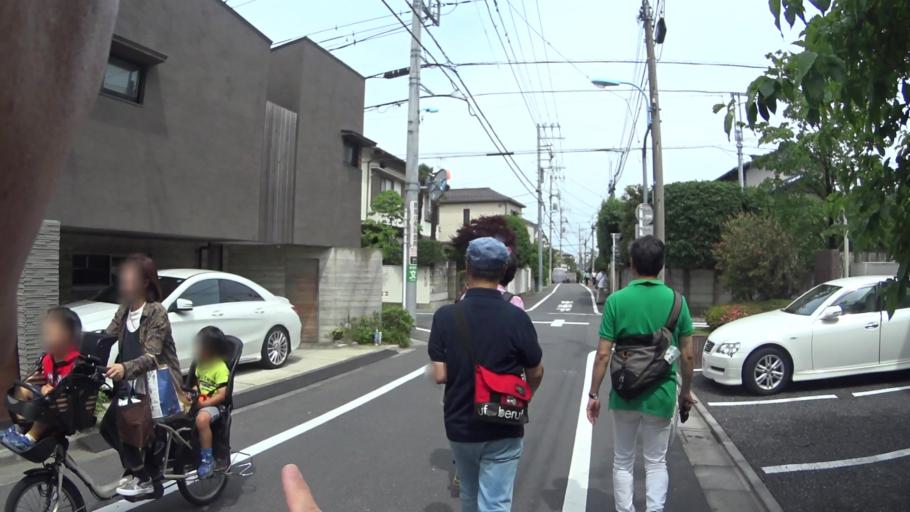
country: JP
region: Tokyo
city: Musashino
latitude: 35.7073
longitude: 139.6037
